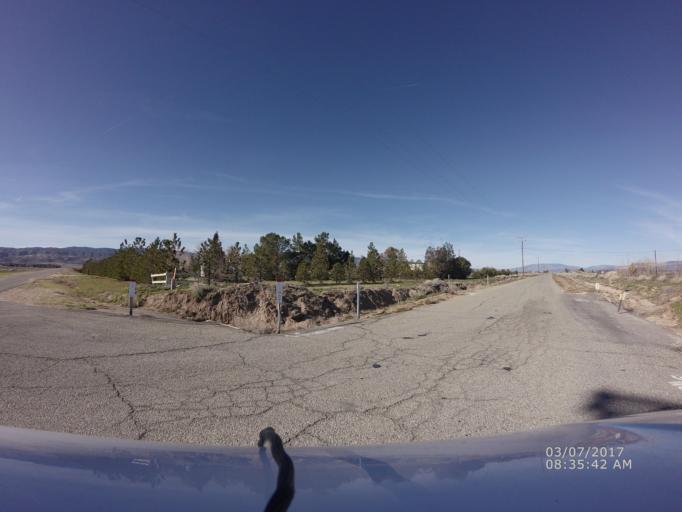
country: US
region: California
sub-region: Los Angeles County
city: Green Valley
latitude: 34.7892
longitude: -118.5371
